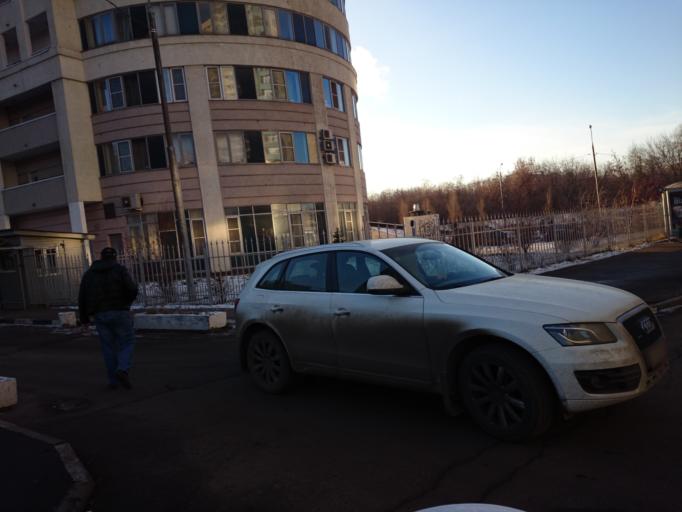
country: RU
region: Moscow
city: Sokol
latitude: 55.7898
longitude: 37.5195
